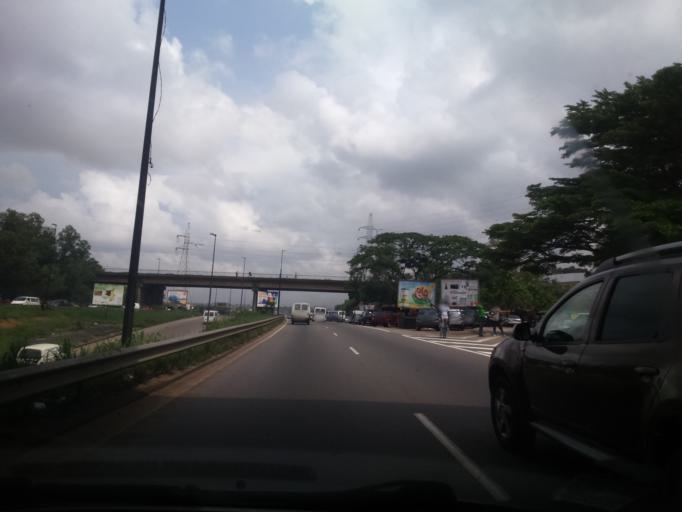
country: CI
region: Lagunes
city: Abobo
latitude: 5.3649
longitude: -4.0294
